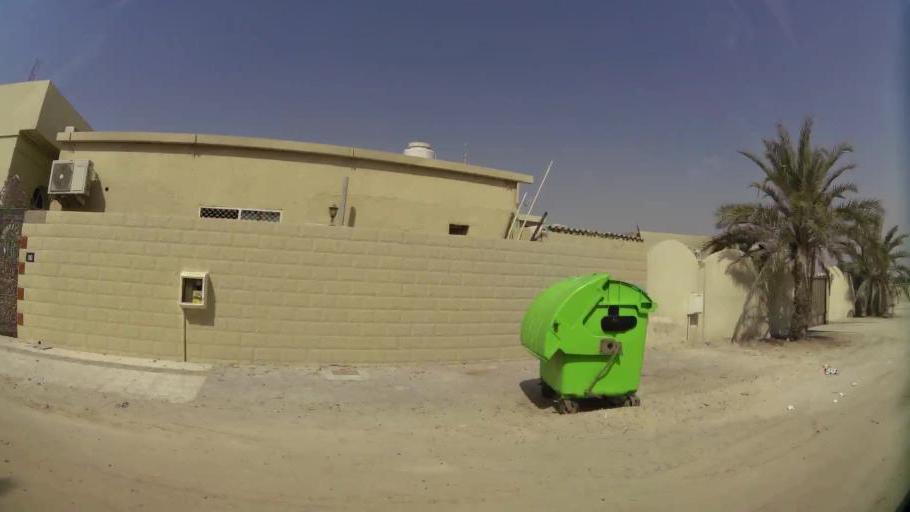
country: AE
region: Ajman
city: Ajman
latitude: 25.3850
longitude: 55.4182
